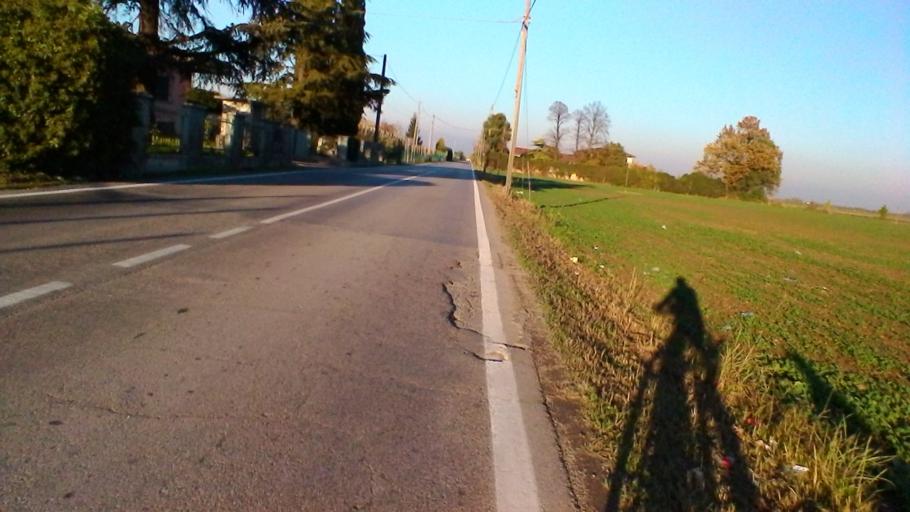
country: IT
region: Veneto
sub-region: Provincia di Verona
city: Povegliano Veronese
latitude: 45.3566
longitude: 10.9005
